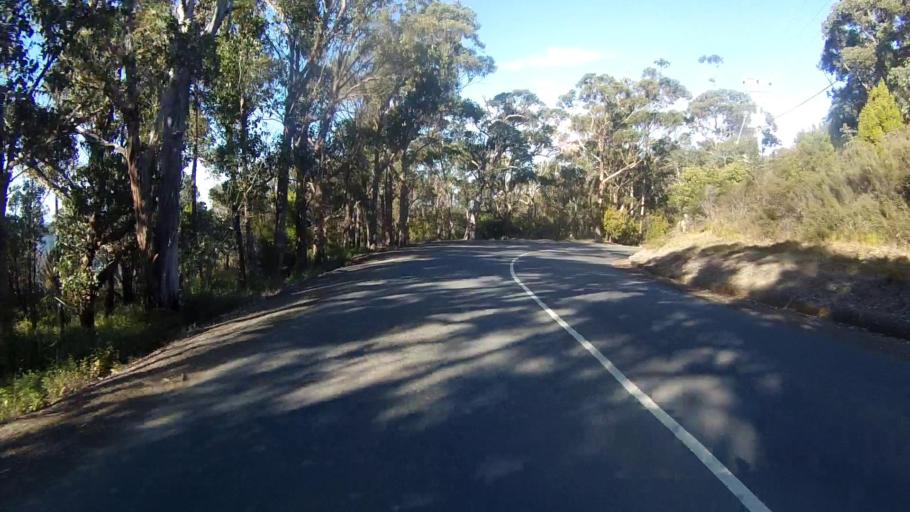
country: AU
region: Tasmania
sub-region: Clarence
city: Sandford
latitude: -43.0283
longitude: 147.9271
